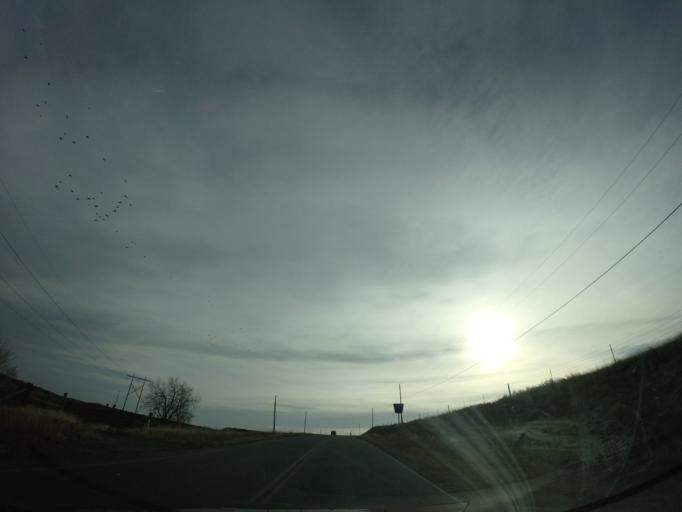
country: US
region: Montana
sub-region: Yellowstone County
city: Billings
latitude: 45.7922
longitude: -108.4555
